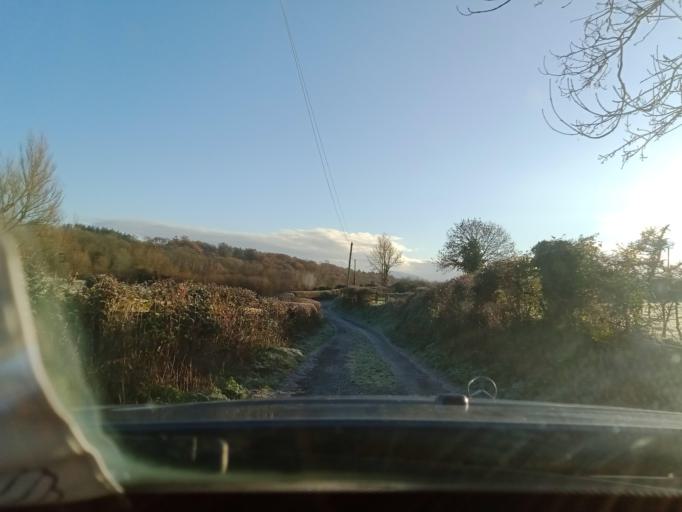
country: IE
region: Leinster
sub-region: Kilkenny
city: Graiguenamanagh
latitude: 52.5982
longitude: -6.9513
